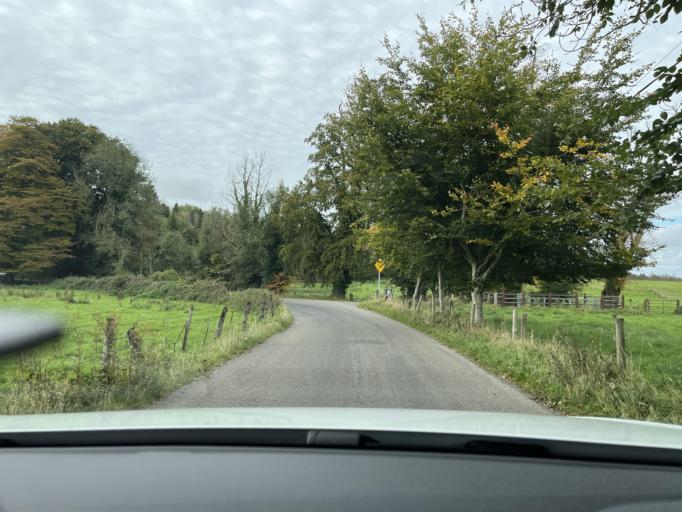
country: IE
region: Connaught
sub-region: Roscommon
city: Boyle
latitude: 53.9772
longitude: -8.2596
